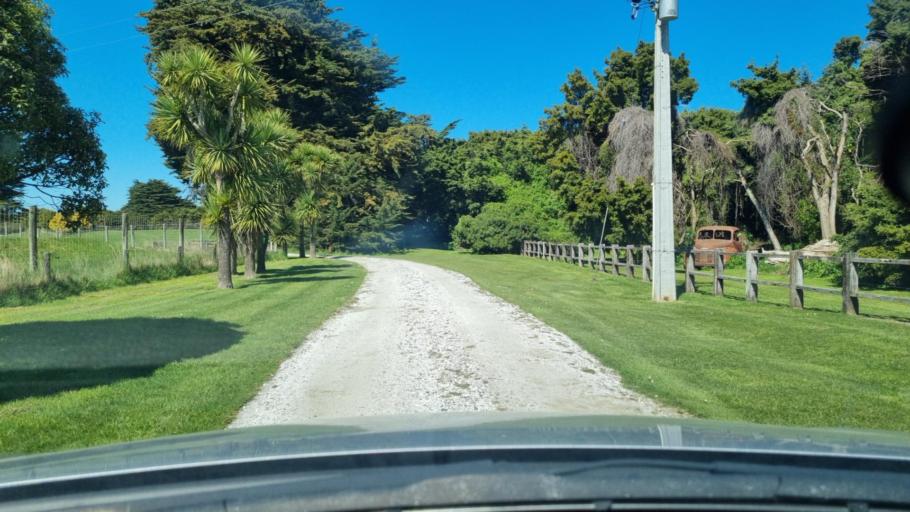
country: NZ
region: Southland
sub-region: Invercargill City
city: Invercargill
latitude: -46.4570
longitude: 168.2813
